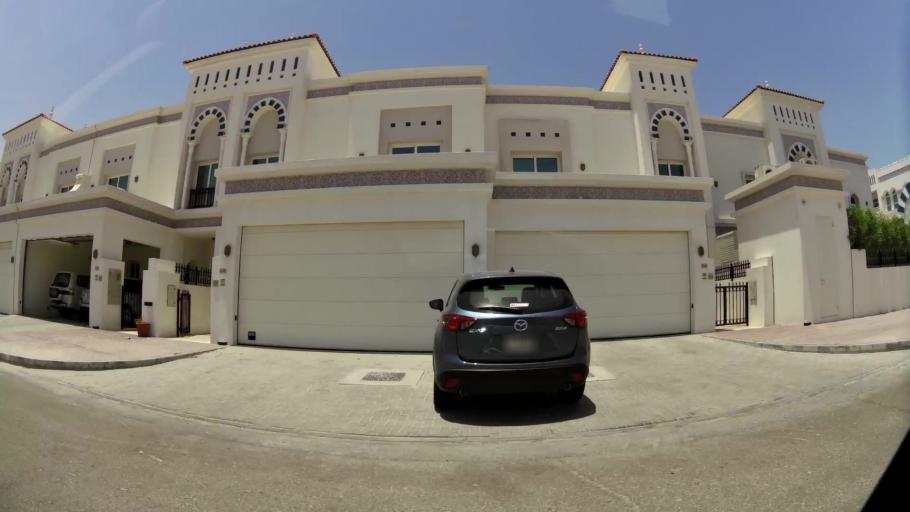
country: AE
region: Dubai
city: Dubai
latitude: 25.1931
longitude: 55.2462
